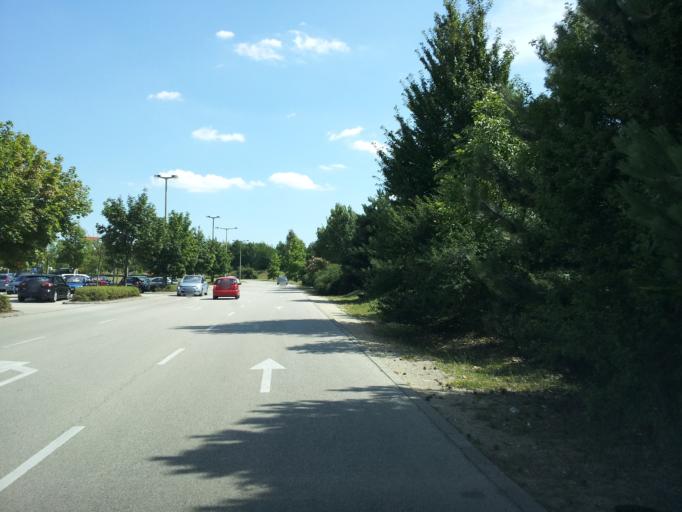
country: HU
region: Veszprem
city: Veszprem
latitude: 47.1025
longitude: 17.9318
